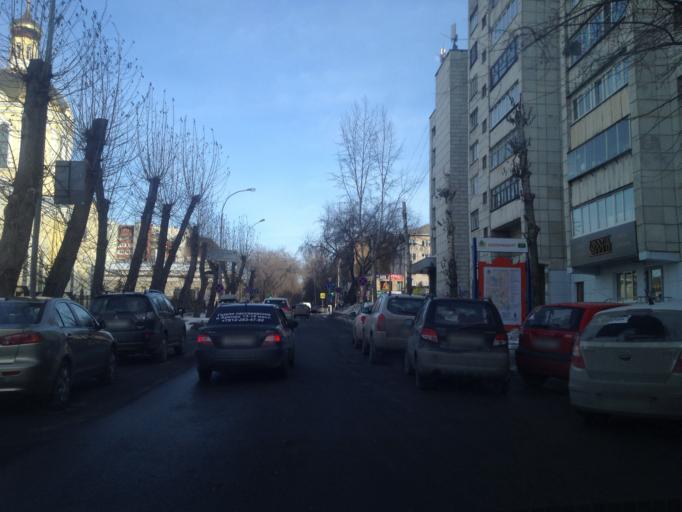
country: RU
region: Sverdlovsk
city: Yekaterinburg
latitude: 56.8316
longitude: 60.6215
